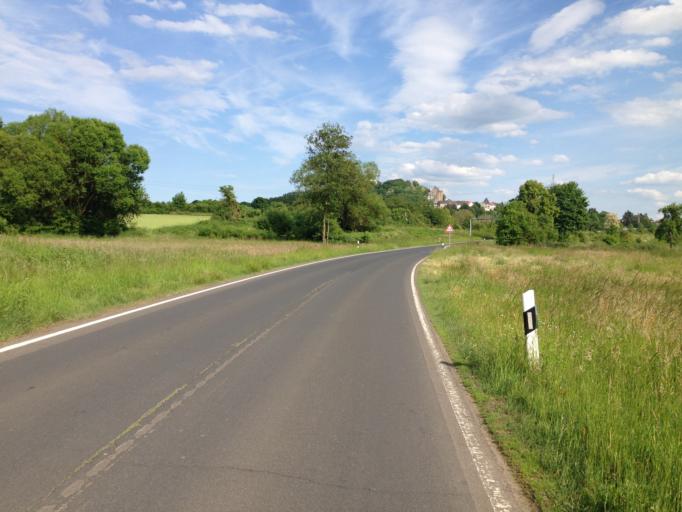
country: DE
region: Hesse
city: Staufenberg
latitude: 50.6691
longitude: 8.7154
